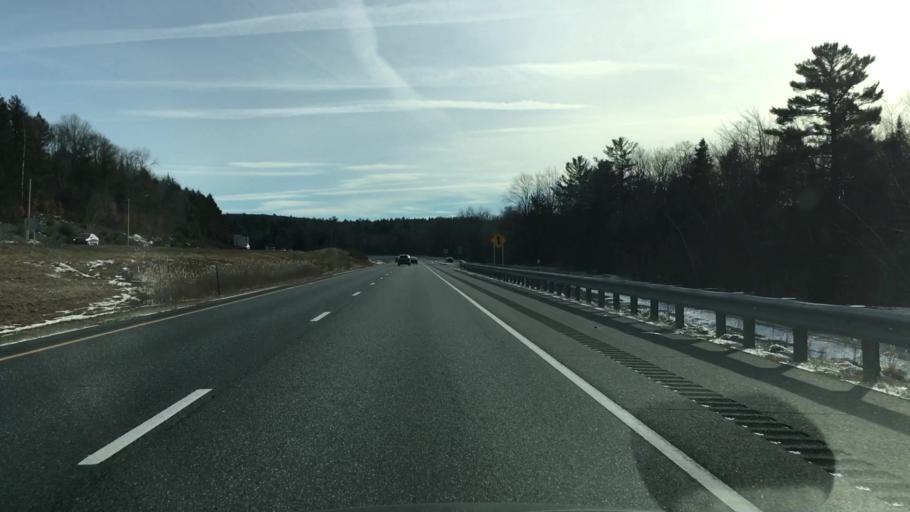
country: US
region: New Hampshire
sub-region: Sullivan County
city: Grantham
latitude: 43.4968
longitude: -72.1324
